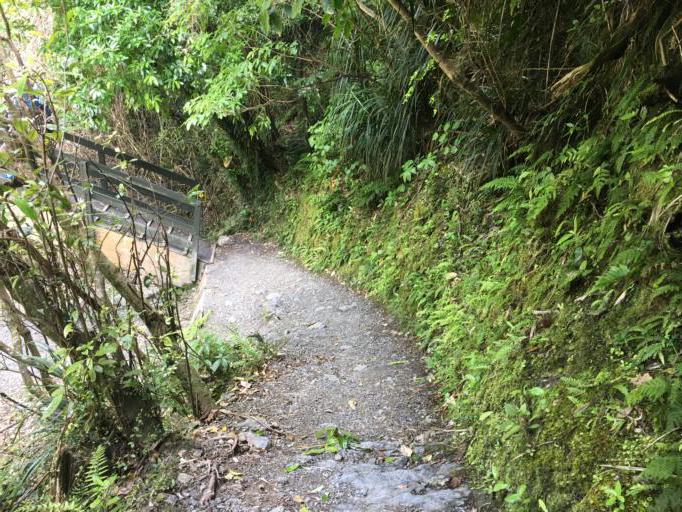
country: NZ
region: Wellington
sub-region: Lower Hutt City
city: Lower Hutt
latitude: -41.3406
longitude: 174.9767
